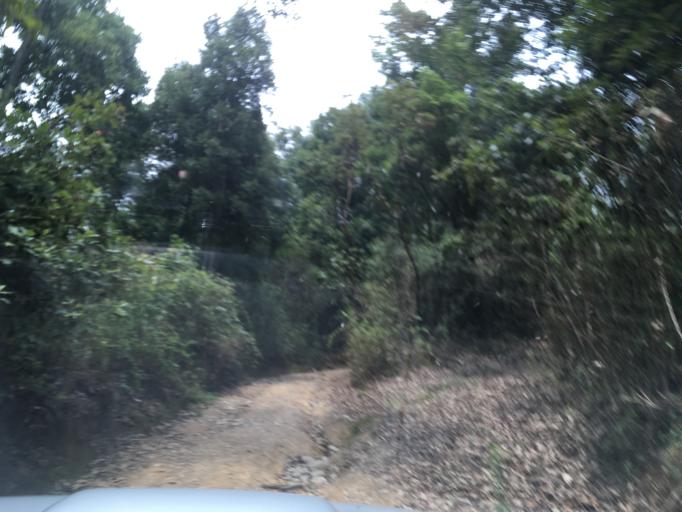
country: MX
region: Michoacan
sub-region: Zitacuaro
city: Macutzio
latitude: 19.5078
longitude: -100.3233
